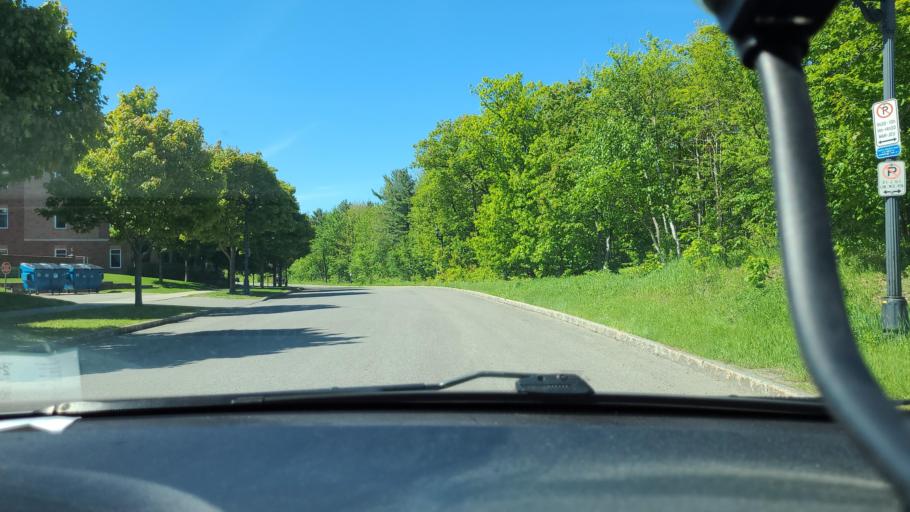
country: CA
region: Quebec
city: L'Ancienne-Lorette
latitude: 46.7543
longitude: -71.3244
